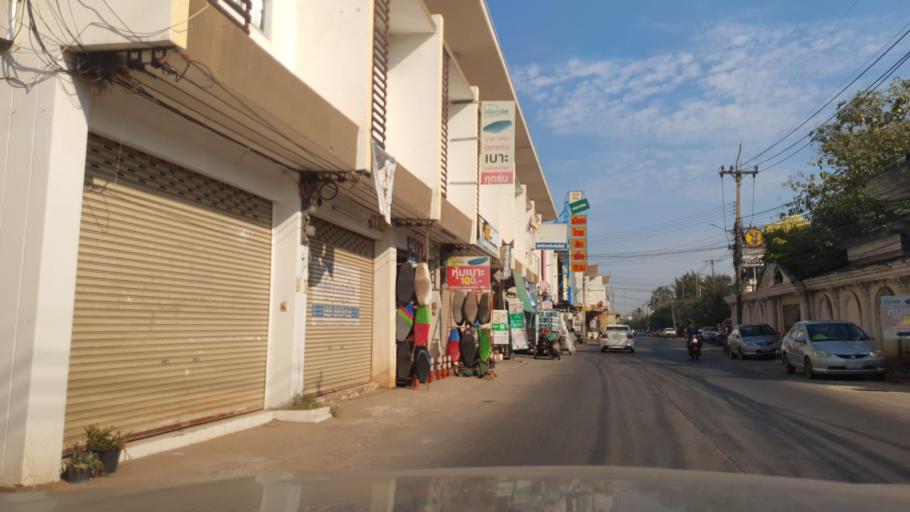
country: TH
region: Khon Kaen
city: Khon Kaen
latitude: 16.4225
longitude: 102.8246
